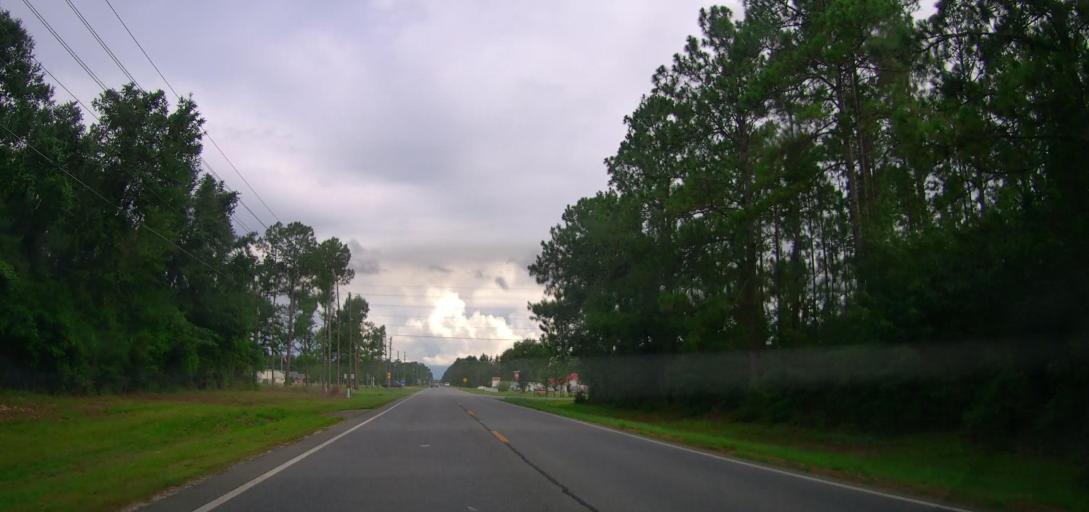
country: US
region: Georgia
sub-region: Wayne County
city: Jesup
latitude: 31.6453
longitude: -81.9075
